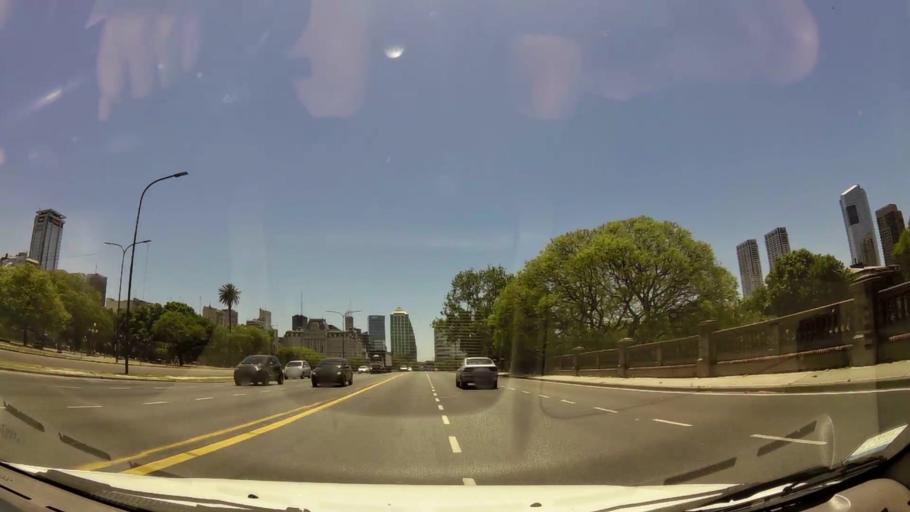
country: AR
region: Buenos Aires F.D.
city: Buenos Aires
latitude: -34.6086
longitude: -58.3675
